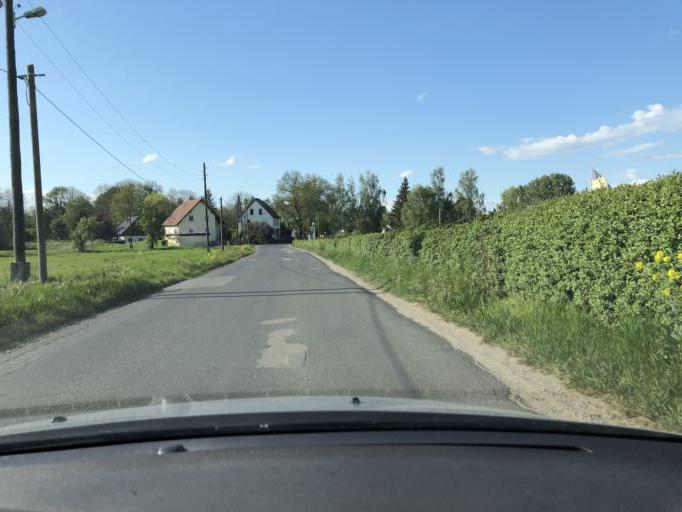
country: DE
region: Thuringia
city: Gerstenberg
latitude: 51.0157
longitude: 12.4368
